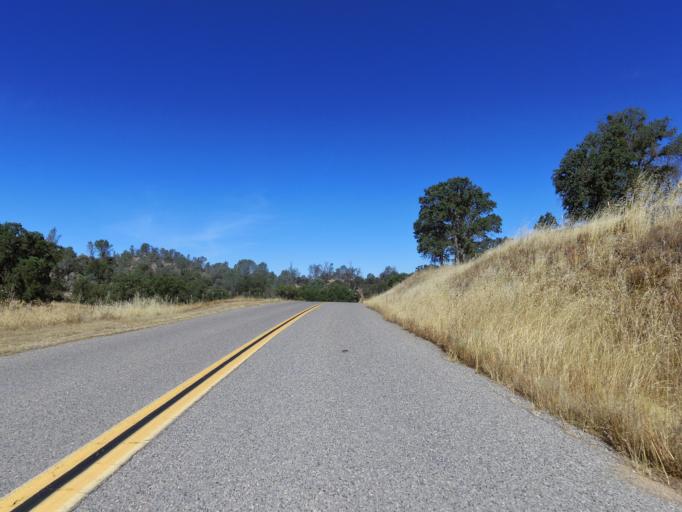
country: US
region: California
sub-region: Madera County
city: Yosemite Lakes
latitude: 37.2581
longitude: -119.9518
